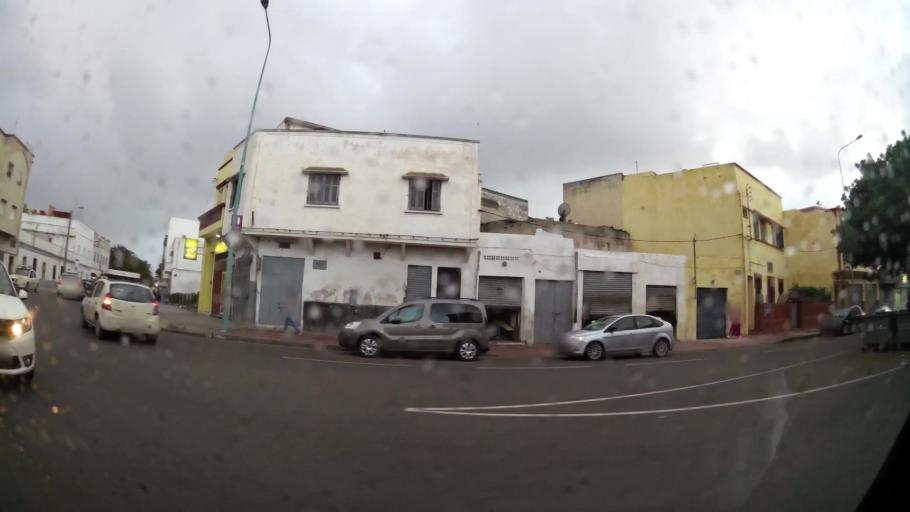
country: MA
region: Doukkala-Abda
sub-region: El-Jadida
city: El Jadida
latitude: 33.2593
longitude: -8.5065
